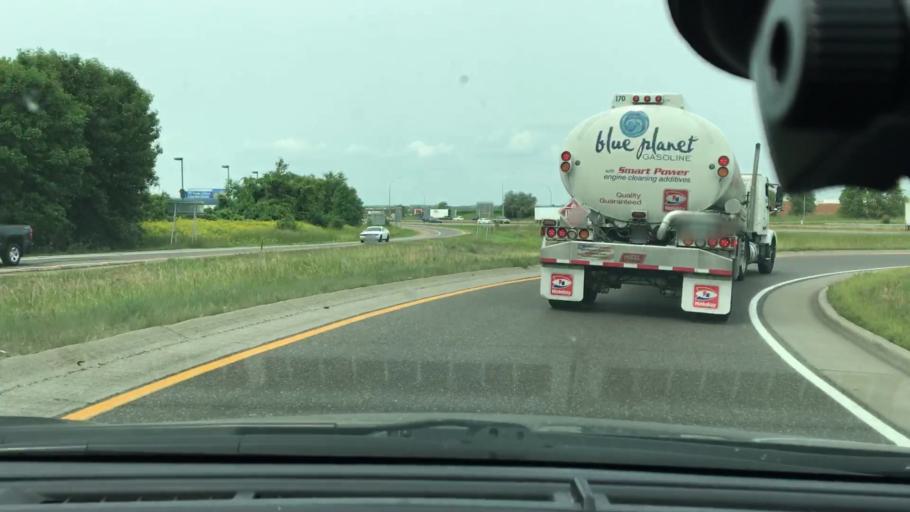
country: US
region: Minnesota
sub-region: Hennepin County
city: Rogers
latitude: 45.1942
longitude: -93.5540
